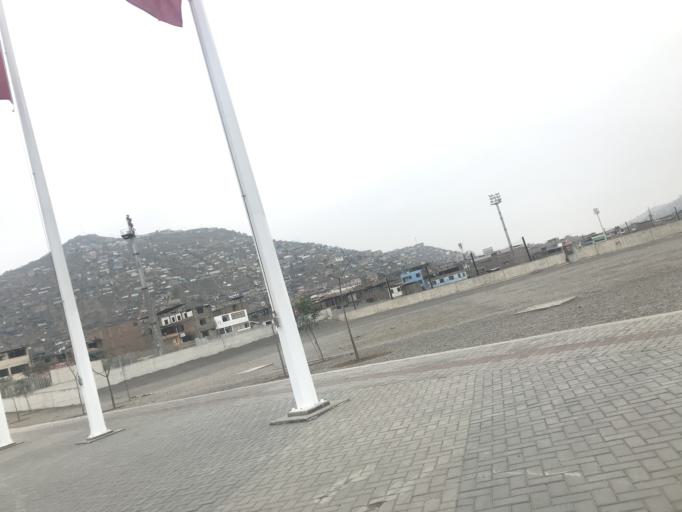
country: PE
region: Lima
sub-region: Lima
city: Surco
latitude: -12.1489
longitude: -76.9524
